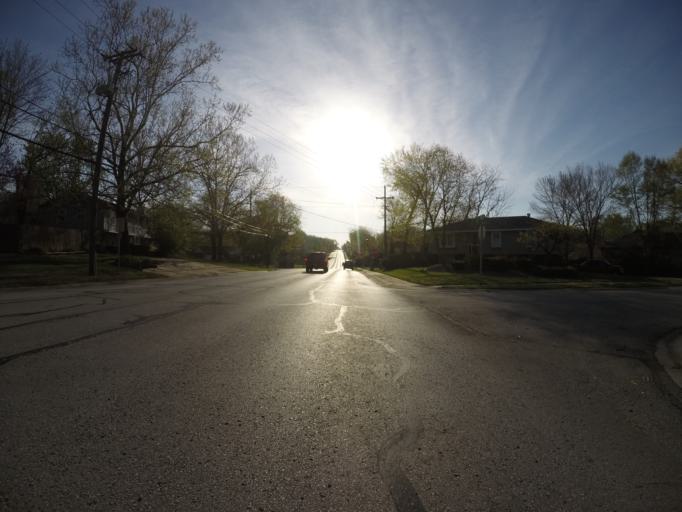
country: US
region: Missouri
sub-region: Jackson County
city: Lees Summit
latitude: 38.9115
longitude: -94.4050
